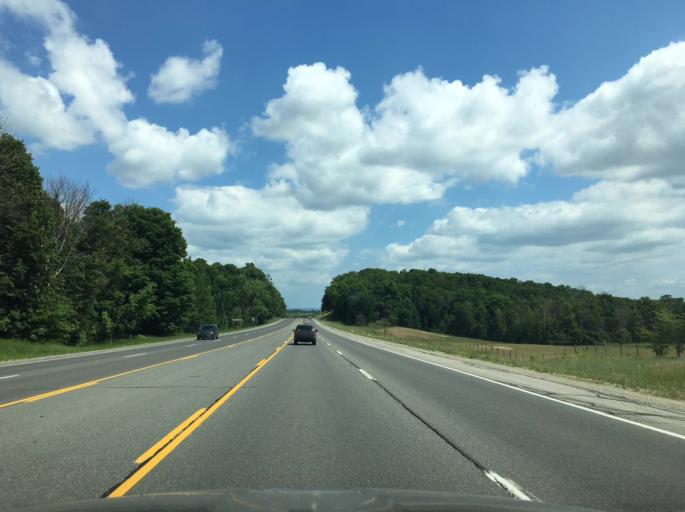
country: US
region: Michigan
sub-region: Grand Traverse County
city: Traverse City
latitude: 44.7088
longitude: -85.6514
